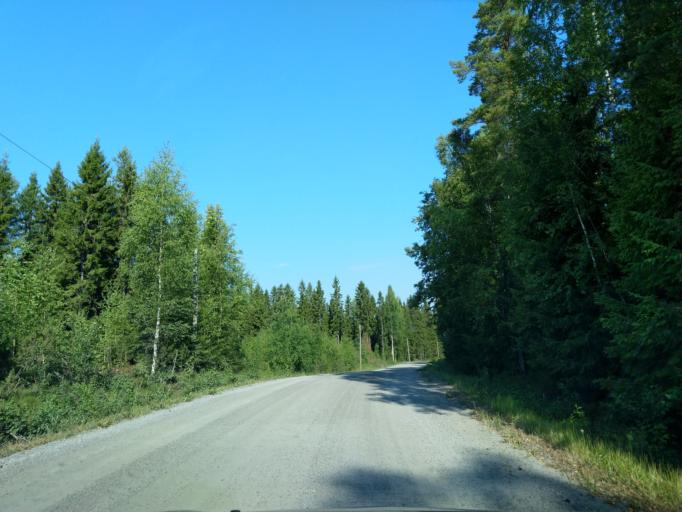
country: FI
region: Satakunta
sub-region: Pori
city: Laengelmaeki
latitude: 61.7259
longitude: 22.1888
